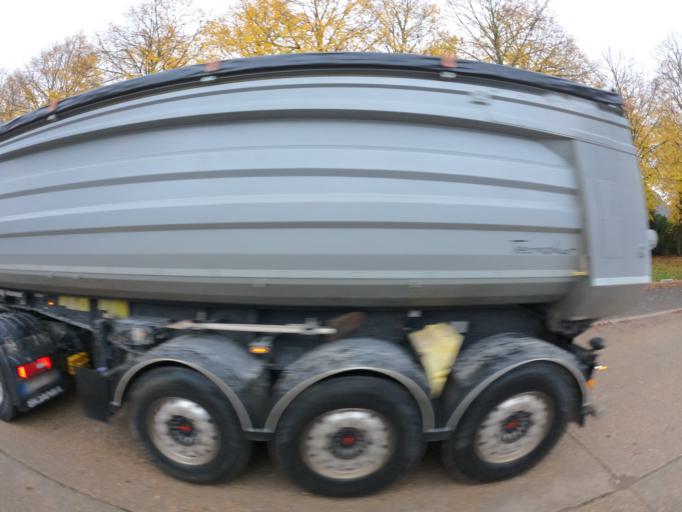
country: FR
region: Ile-de-France
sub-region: Departement du Val-de-Marne
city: Chennevieres-sur-Marne
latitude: 48.7946
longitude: 2.5471
